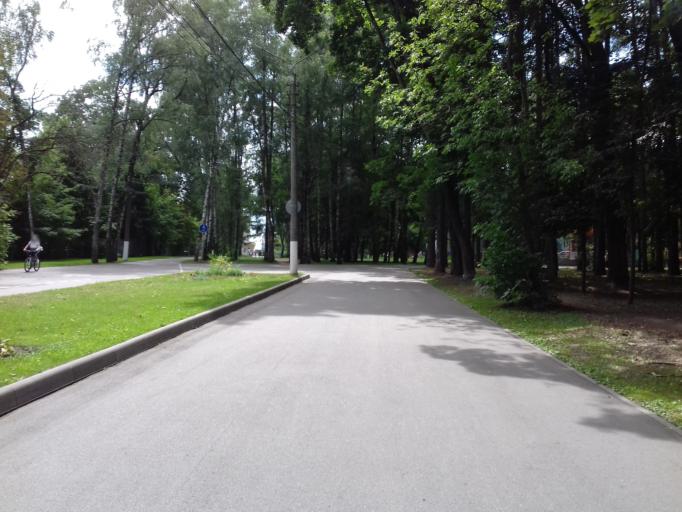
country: RU
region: Tula
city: Tula
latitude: 54.1813
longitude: 37.5960
